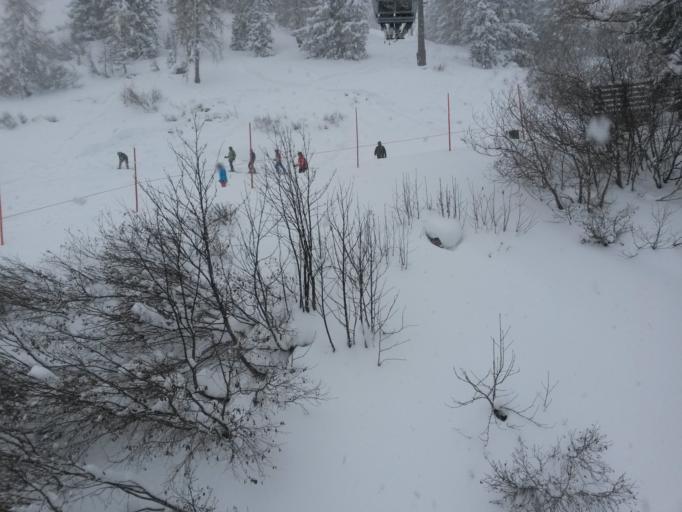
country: AT
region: Salzburg
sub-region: Politischer Bezirk Sankt Johann im Pongau
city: Dorfgastein
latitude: 47.2312
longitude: 13.1582
